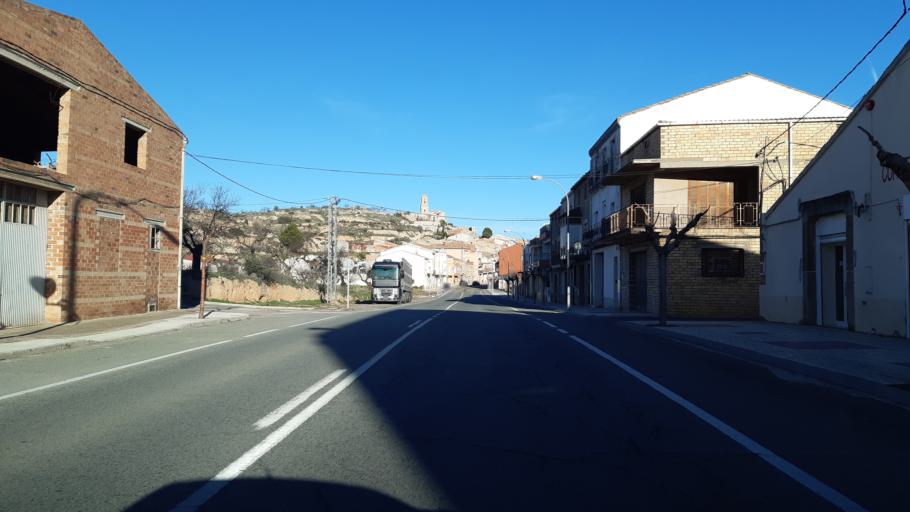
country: ES
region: Catalonia
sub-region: Provincia de Tarragona
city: Gandesa
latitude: 41.0745
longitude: 0.4696
